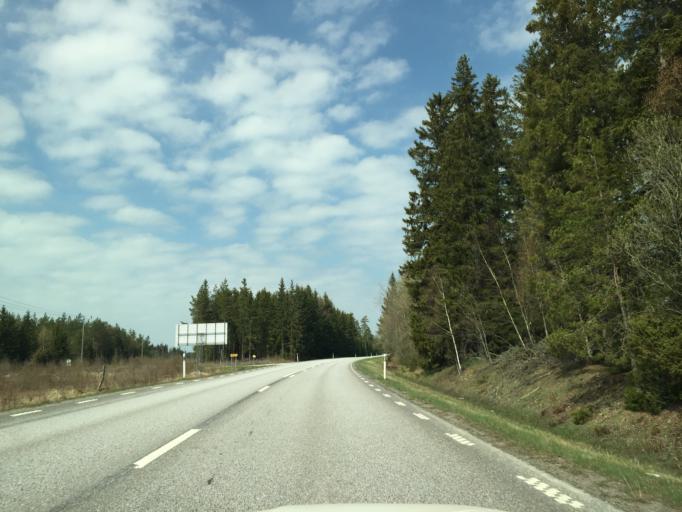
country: SE
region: Vaestra Goetaland
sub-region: Bengtsfors Kommun
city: Dals Langed
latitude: 58.8055
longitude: 12.1501
